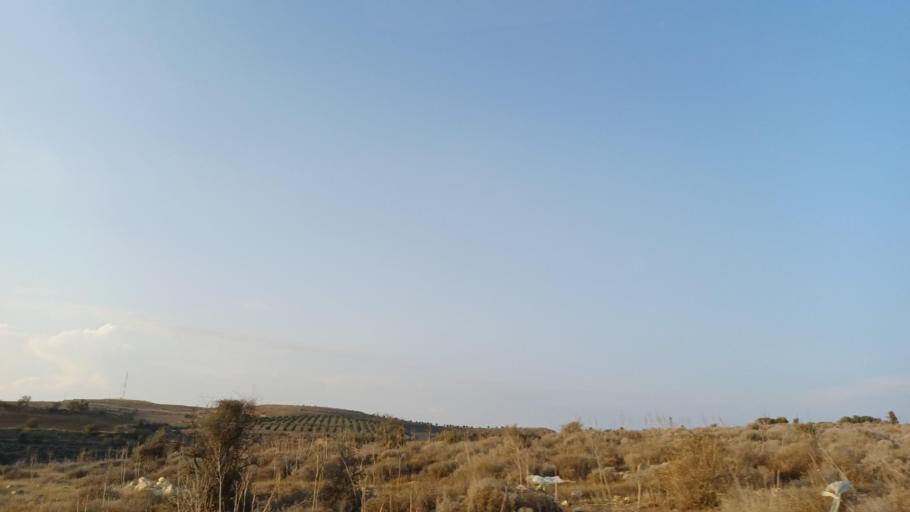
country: CY
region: Larnaka
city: Athienou
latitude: 35.0191
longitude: 33.5431
